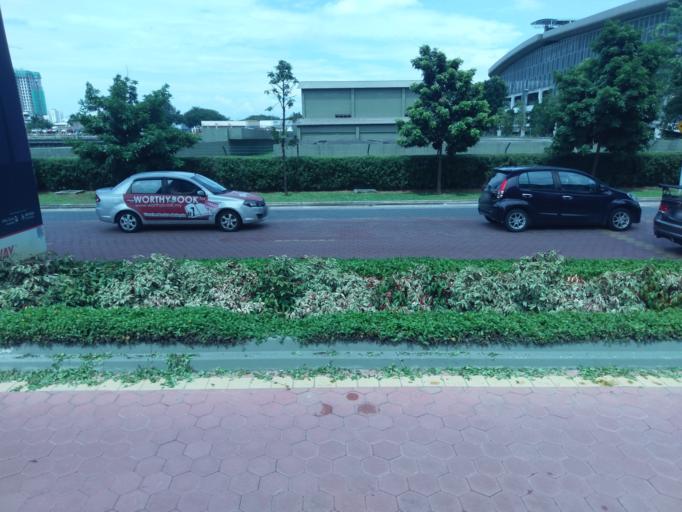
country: MY
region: Selangor
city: Subang Jaya
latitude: 3.0653
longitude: 101.6001
